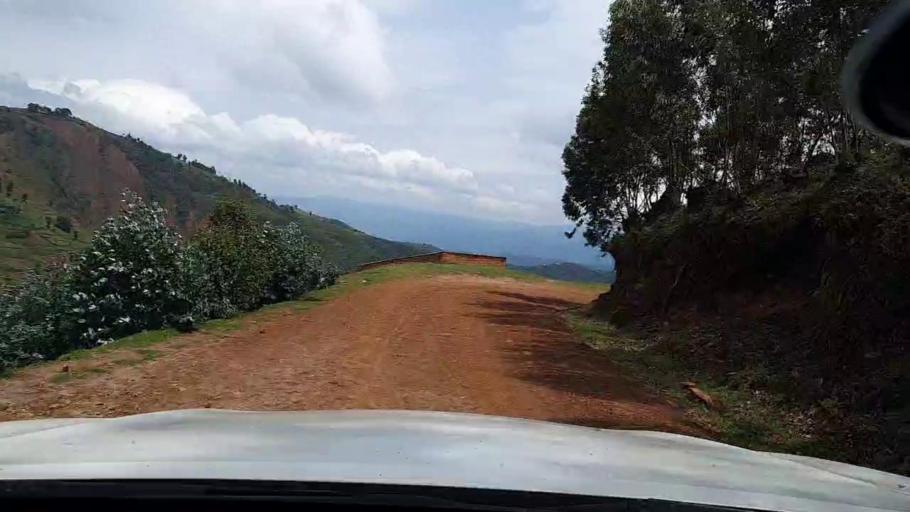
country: RW
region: Western Province
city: Kibuye
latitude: -2.1652
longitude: 29.3999
